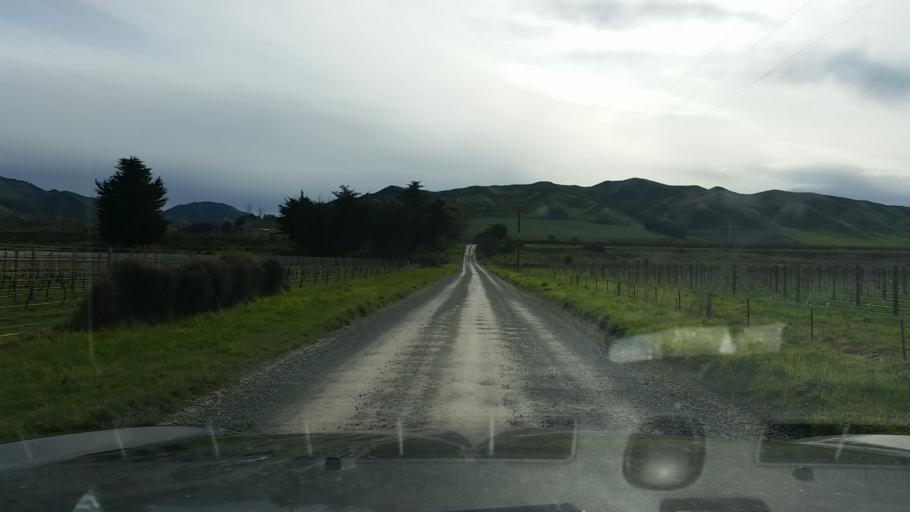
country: NZ
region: Marlborough
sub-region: Marlborough District
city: Blenheim
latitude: -41.6494
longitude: 174.0554
